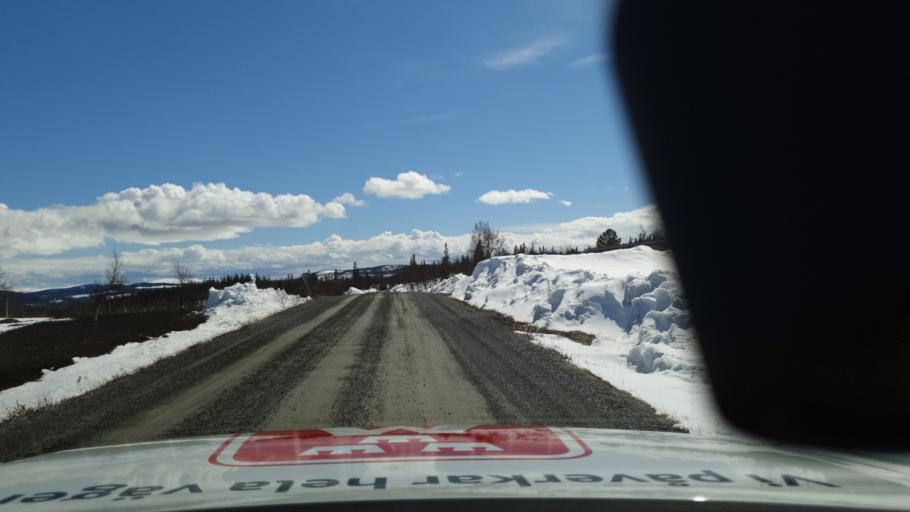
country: SE
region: Jaemtland
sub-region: Are Kommun
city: Are
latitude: 62.8832
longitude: 12.7255
